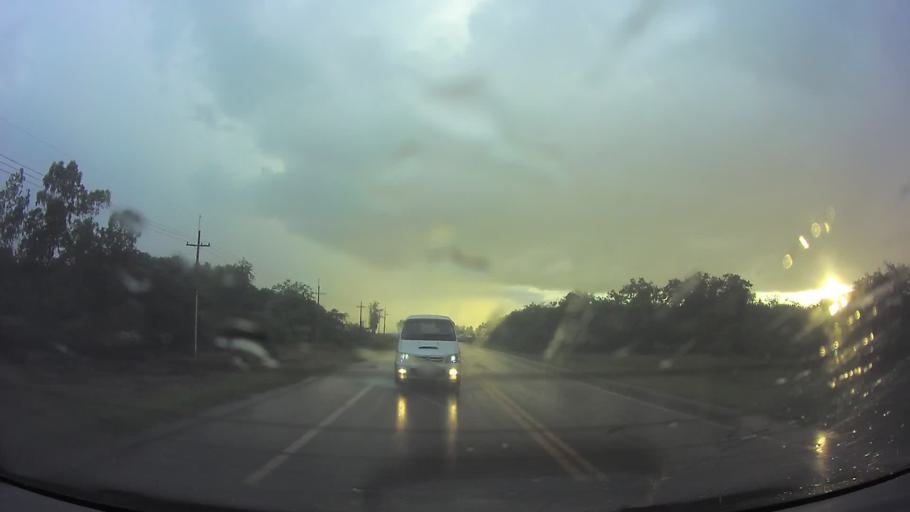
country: PY
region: Paraguari
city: Paraguari
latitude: -25.6455
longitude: -57.1580
